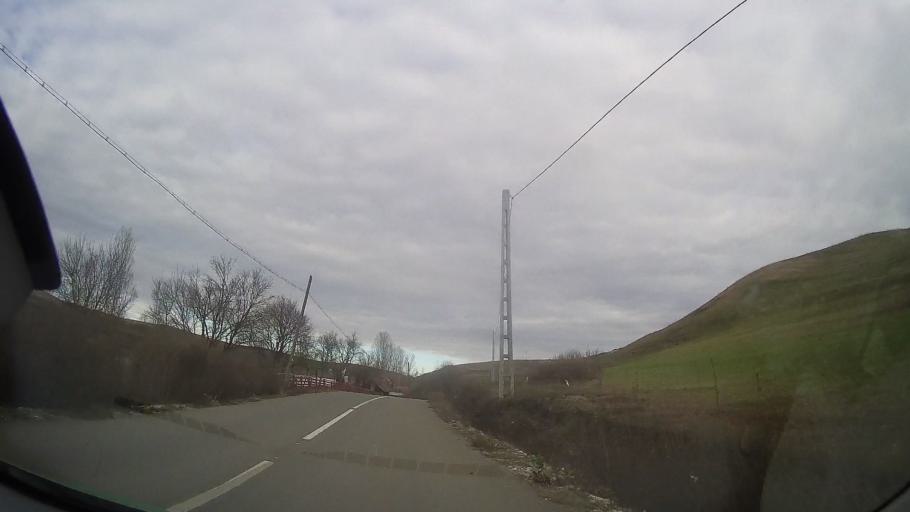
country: RO
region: Bistrita-Nasaud
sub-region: Comuna Silvasu de Campie
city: Silvasu de Campie
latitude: 46.8109
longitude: 24.2952
